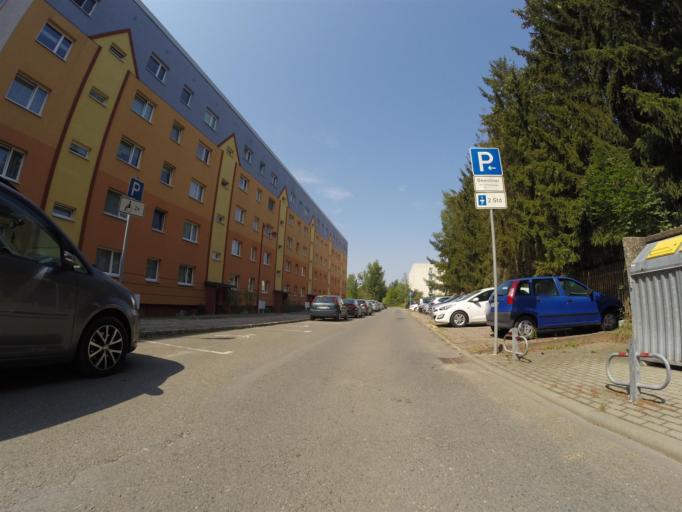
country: DE
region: Thuringia
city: Stadtroda
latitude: 50.8607
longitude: 11.7310
